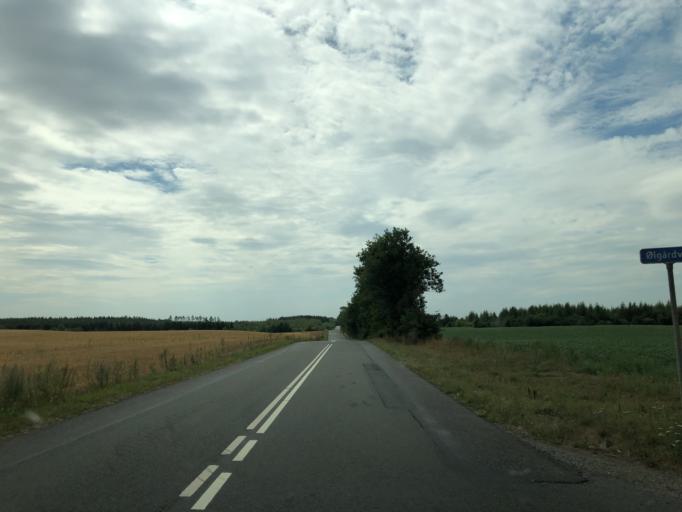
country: DK
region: South Denmark
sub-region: Vejle Kommune
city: Egtved
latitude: 55.6357
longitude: 9.1972
